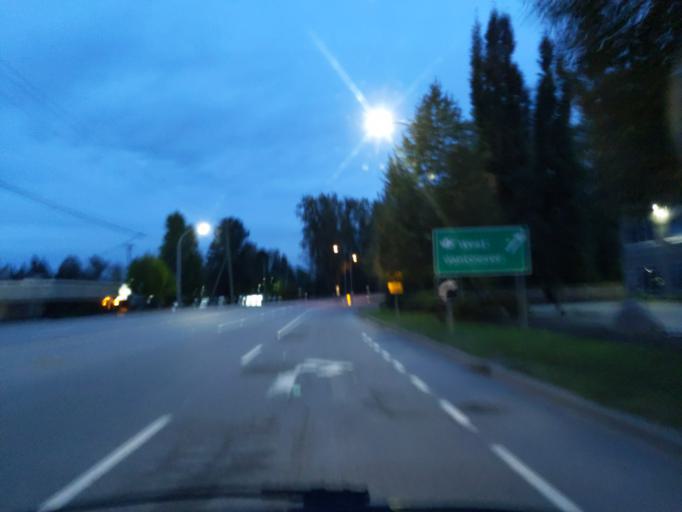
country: CA
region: British Columbia
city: Pitt Meadows
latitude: 49.1728
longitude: -122.6907
